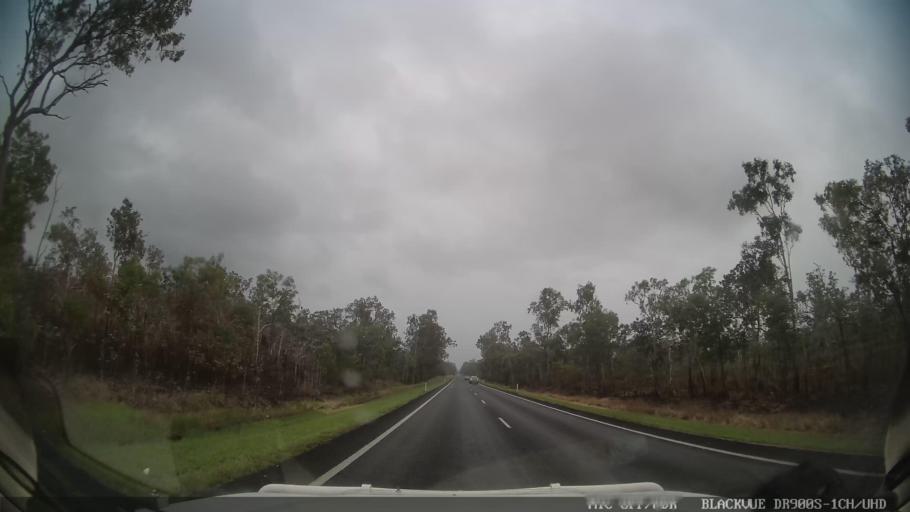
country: AU
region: Queensland
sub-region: Hinchinbrook
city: Ingham
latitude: -18.4346
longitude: 146.1391
